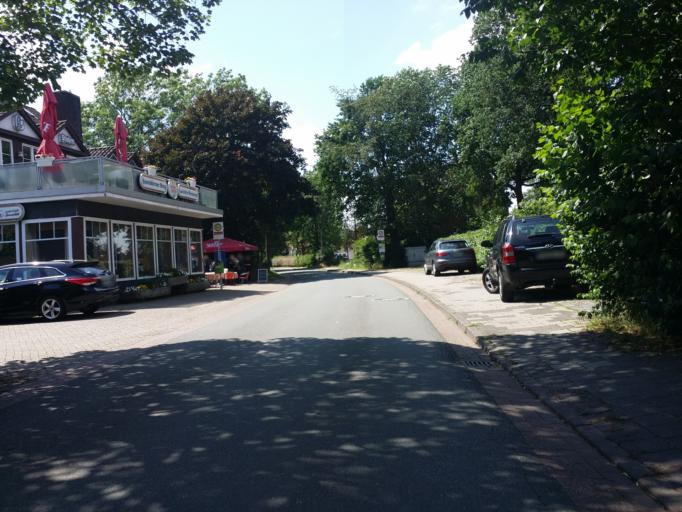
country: DE
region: Lower Saxony
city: Ritterhude
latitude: 53.1168
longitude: 8.7009
